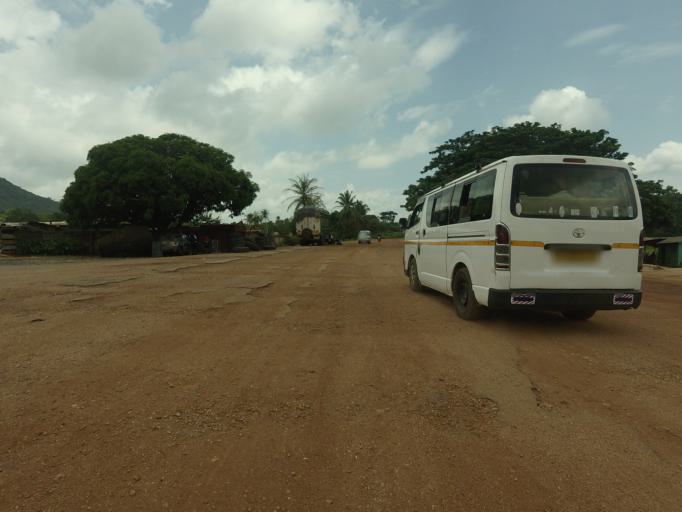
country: GH
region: Volta
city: Ho
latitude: 6.6818
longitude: 0.3311
